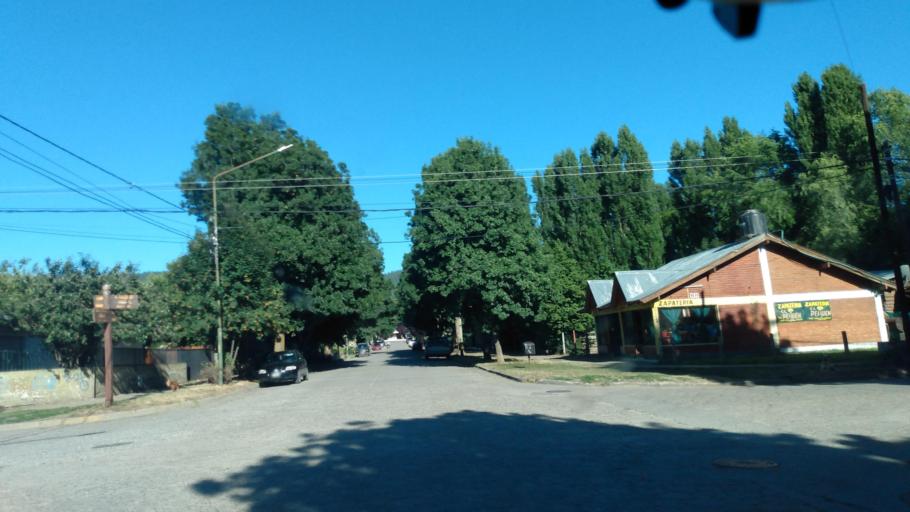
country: AR
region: Neuquen
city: Junin de los Andes
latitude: -39.9520
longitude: -71.0733
